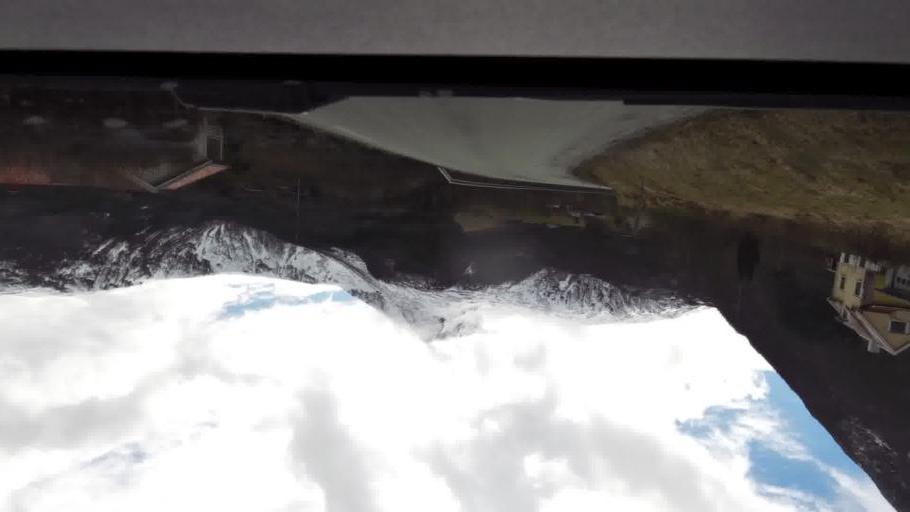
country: NO
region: More og Romsdal
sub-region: Kristiansund
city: Kristiansund
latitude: 63.1196
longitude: 7.7472
